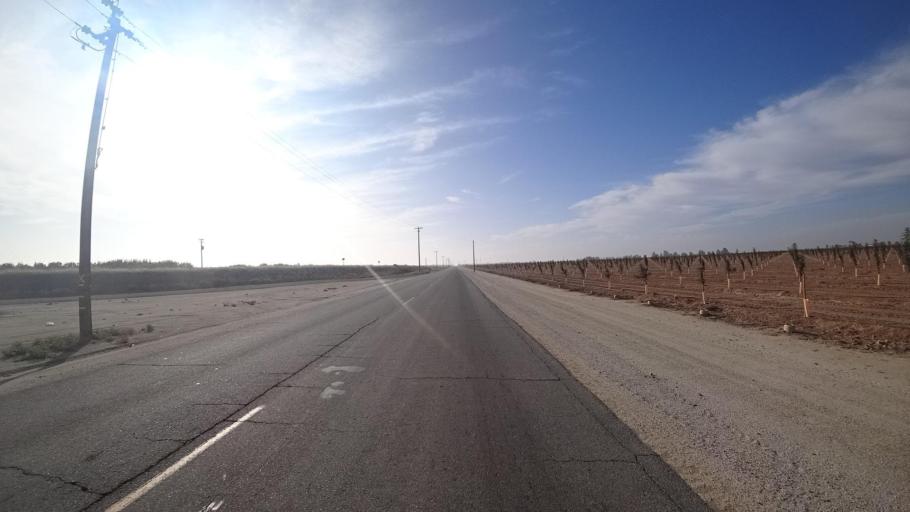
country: US
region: California
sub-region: Kern County
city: McFarland
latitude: 35.6513
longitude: -119.2046
